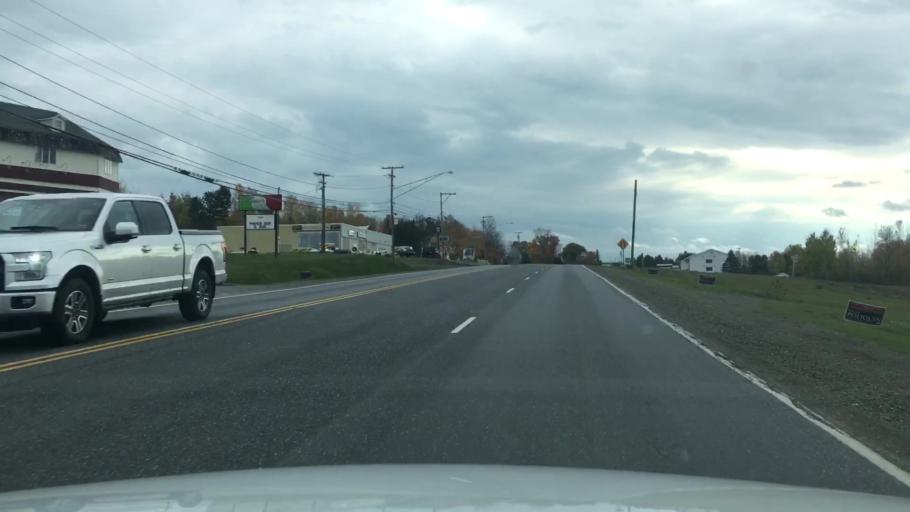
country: US
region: Maine
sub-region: Aroostook County
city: Presque Isle
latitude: 46.6677
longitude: -68.0120
